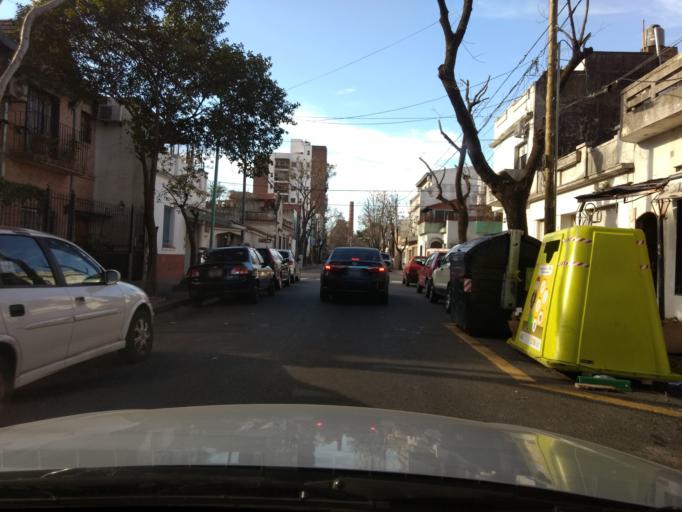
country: AR
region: Buenos Aires F.D.
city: Villa Santa Rita
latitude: -34.6313
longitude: -58.4880
